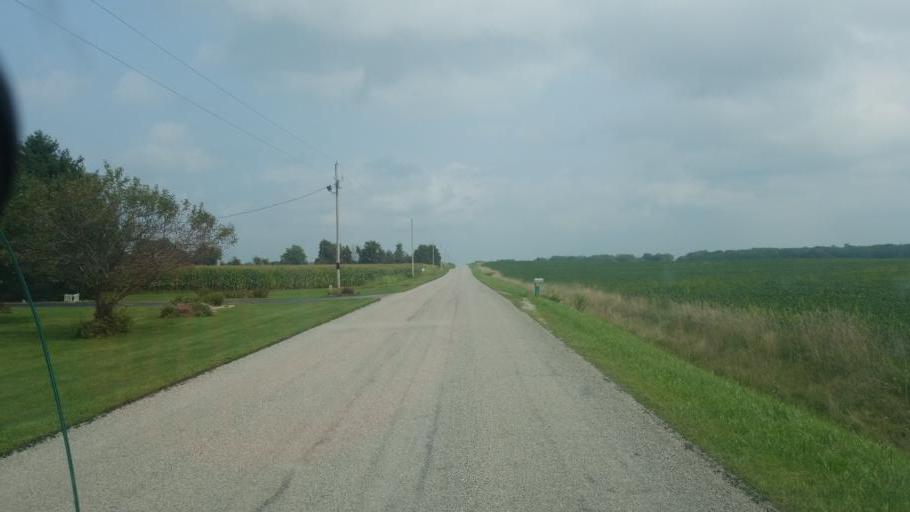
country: US
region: Ohio
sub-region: Huron County
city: Greenwich
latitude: 41.0669
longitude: -82.5537
